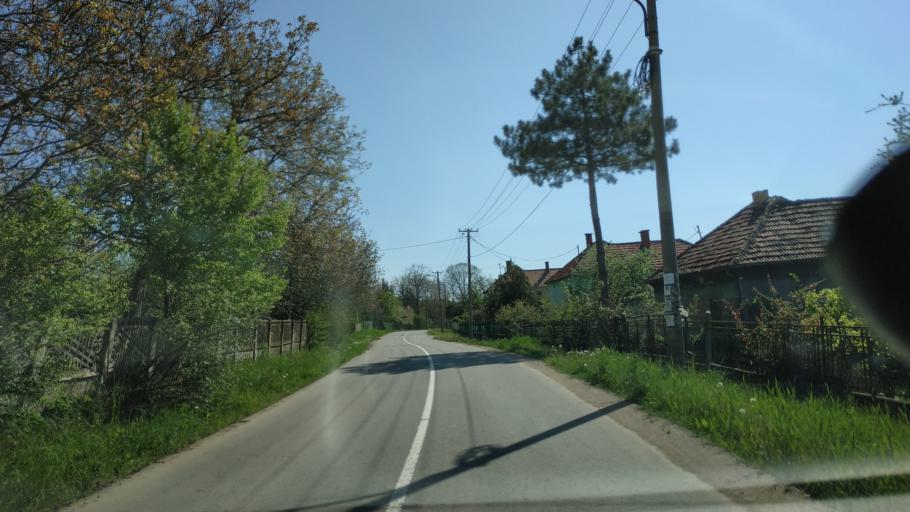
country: RS
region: Central Serbia
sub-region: Nisavski Okrug
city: Nis
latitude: 43.4631
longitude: 21.8614
